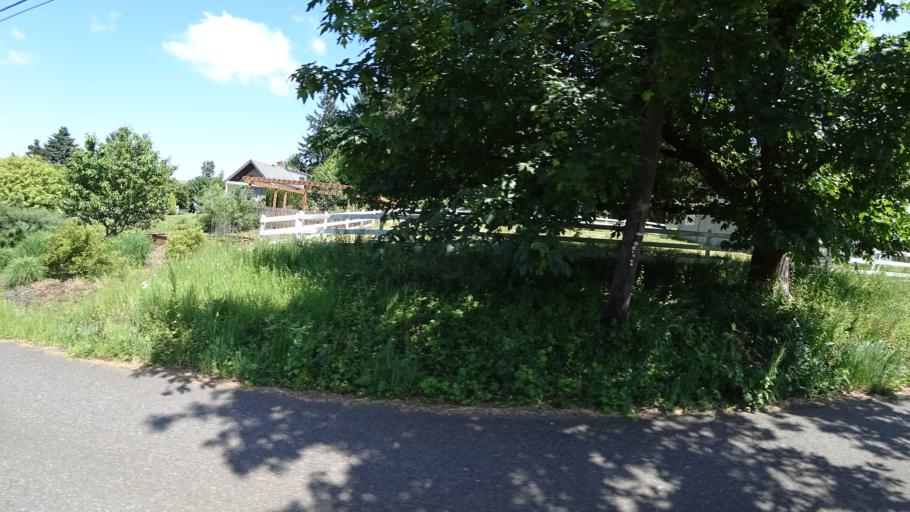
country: US
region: Oregon
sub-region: Clackamas County
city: Lake Oswego
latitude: 45.4346
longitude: -122.6974
